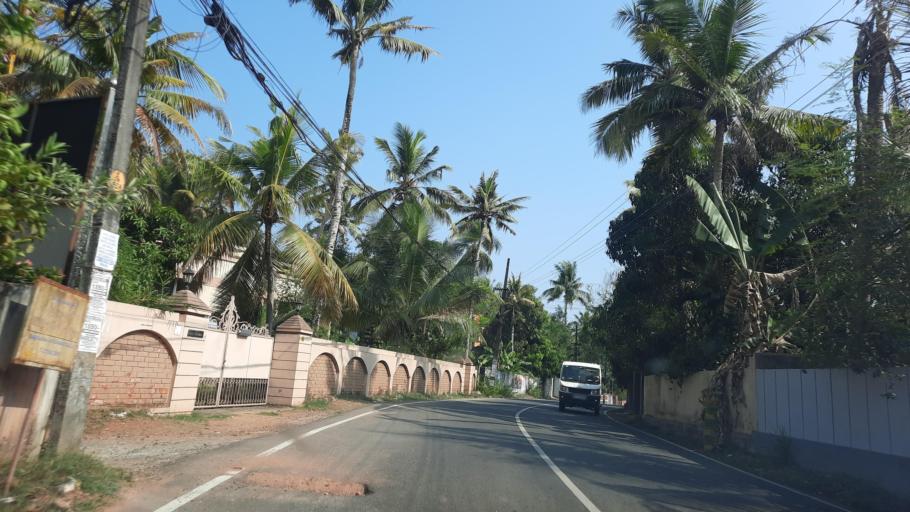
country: IN
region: Kerala
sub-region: Thiruvananthapuram
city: Thiruvananthapuram
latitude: 8.5614
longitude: 76.9211
